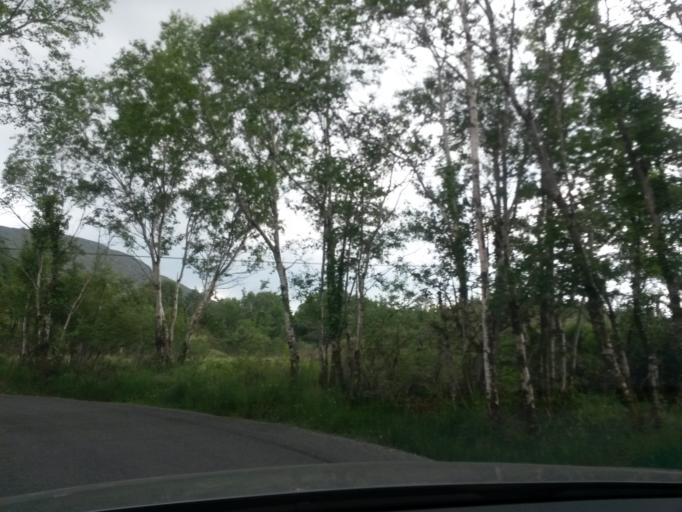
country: IE
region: Munster
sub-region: Ciarrai
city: Kenmare
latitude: 51.8659
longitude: -9.5717
